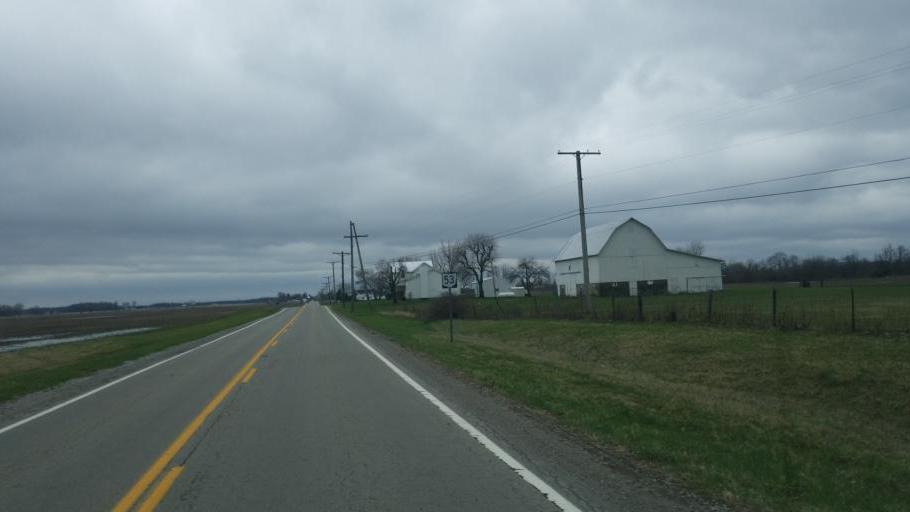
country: US
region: Ohio
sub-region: Hardin County
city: Forest
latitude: 40.7237
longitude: -83.5581
